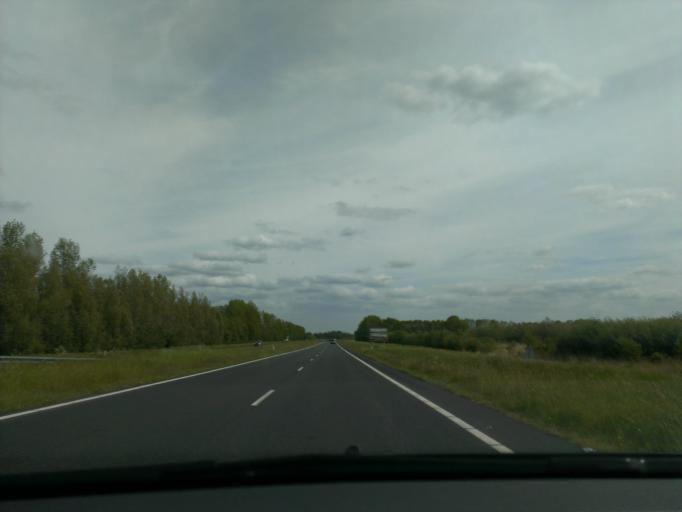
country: NL
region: Gelderland
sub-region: Gemeente Harderwijk
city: Harderwijk
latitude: 52.3793
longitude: 5.5918
